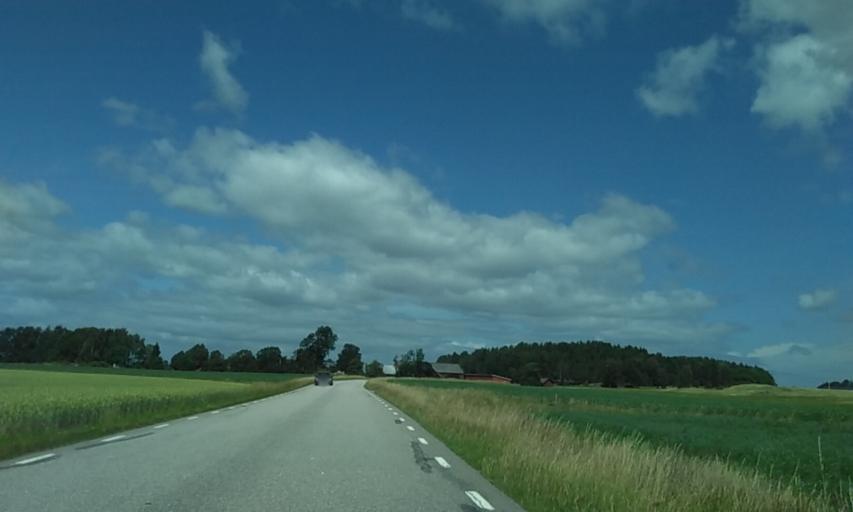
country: SE
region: Vaestra Goetaland
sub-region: Grastorps Kommun
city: Graestorp
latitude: 58.3589
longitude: 12.6787
